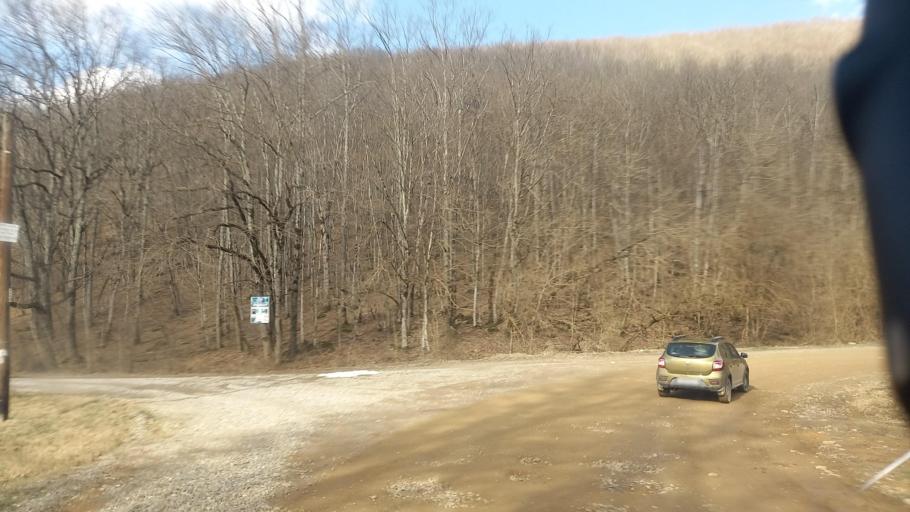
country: RU
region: Krasnodarskiy
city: Smolenskaya
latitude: 44.6052
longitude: 38.8422
